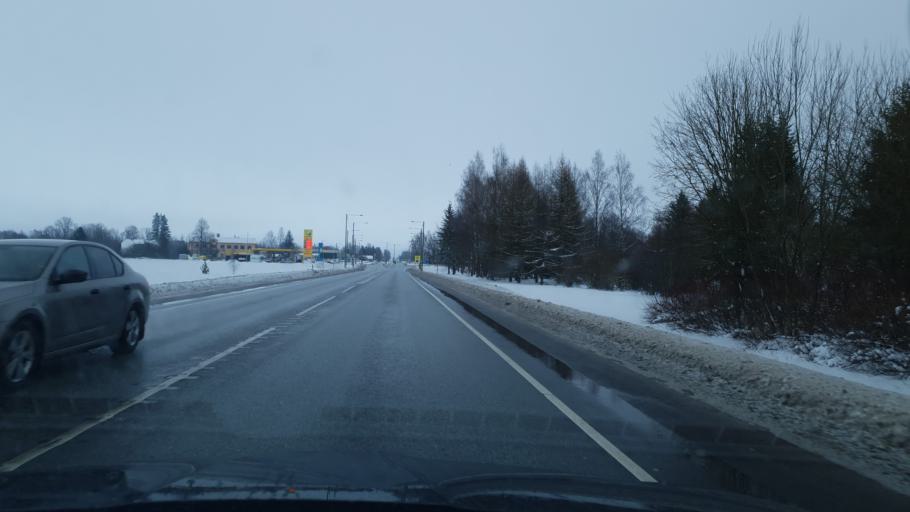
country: EE
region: Jogevamaa
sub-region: Poltsamaa linn
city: Poltsamaa
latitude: 58.6647
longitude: 25.9848
